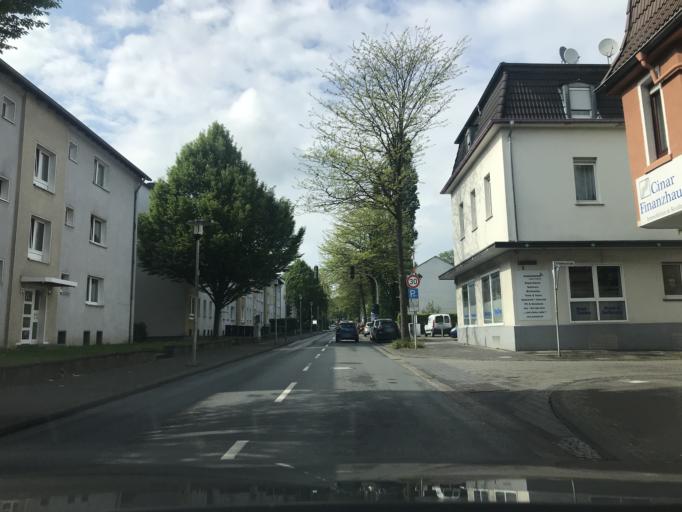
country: DE
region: North Rhine-Westphalia
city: Schwerte
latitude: 51.4387
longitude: 7.5626
